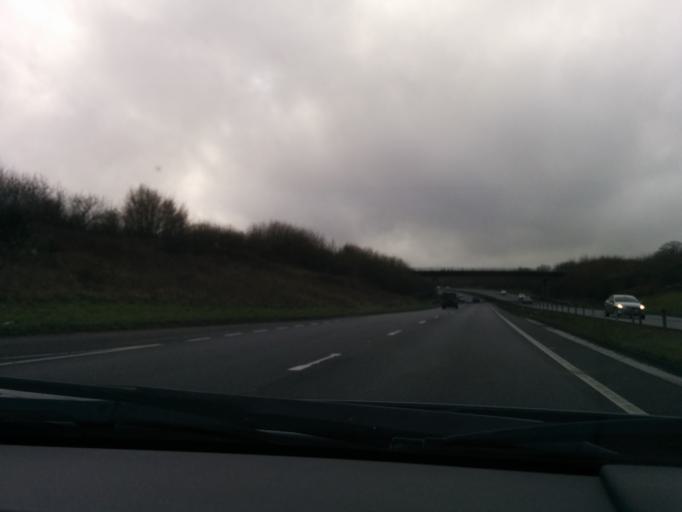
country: GB
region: England
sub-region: Hampshire
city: Highclere
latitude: 51.3745
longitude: -1.3631
